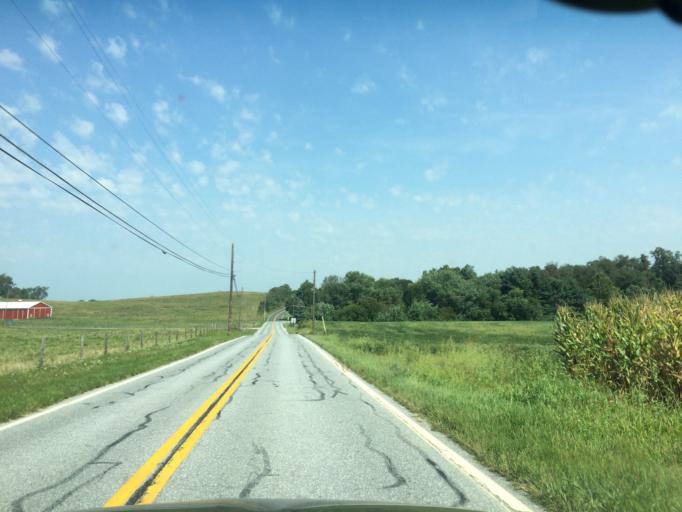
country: US
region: Maryland
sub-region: Carroll County
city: New Windsor
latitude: 39.5993
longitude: -77.1212
